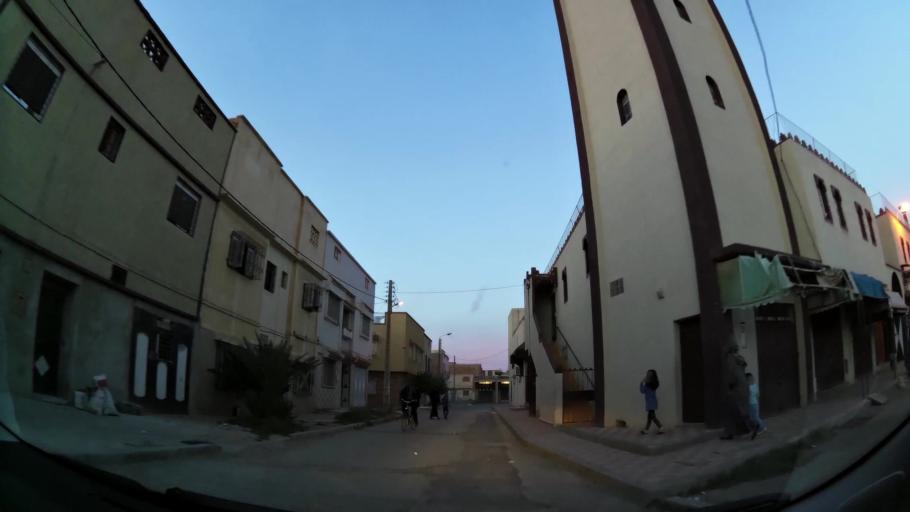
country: MA
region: Oriental
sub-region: Oujda-Angad
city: Oujda
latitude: 34.6827
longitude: -1.8779
